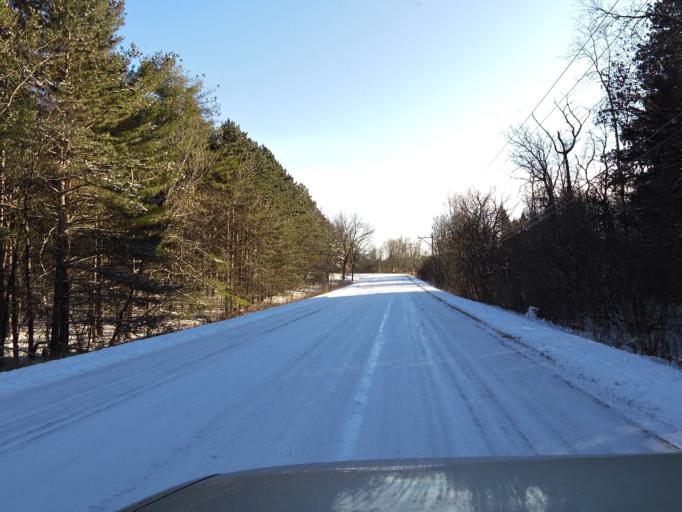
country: US
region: Minnesota
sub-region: Washington County
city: Lake Elmo
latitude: 44.9727
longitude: -92.8608
